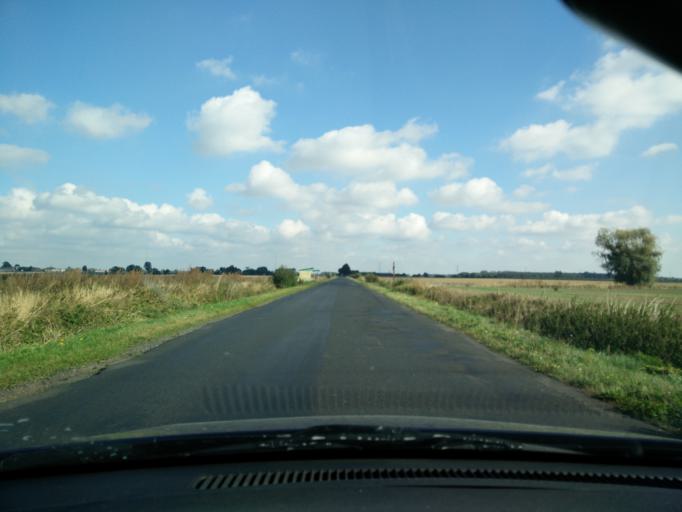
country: PL
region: Greater Poland Voivodeship
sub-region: Powiat sredzki
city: Dominowo
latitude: 52.2826
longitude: 17.3225
